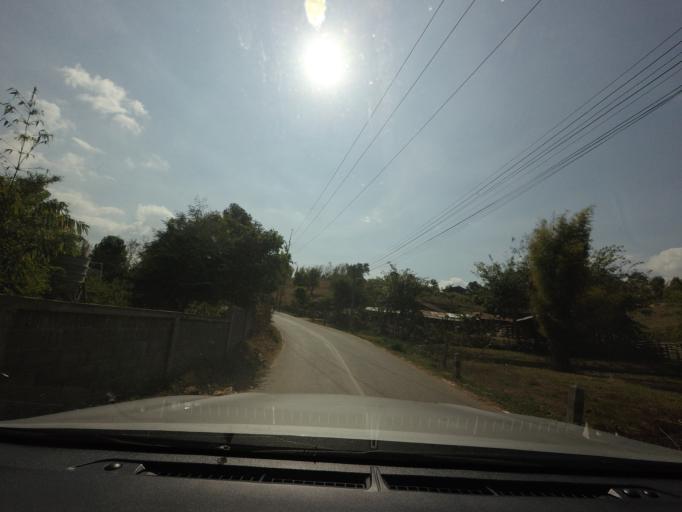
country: TH
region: Mae Hong Son
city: Wiang Nuea
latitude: 19.4008
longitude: 98.4424
